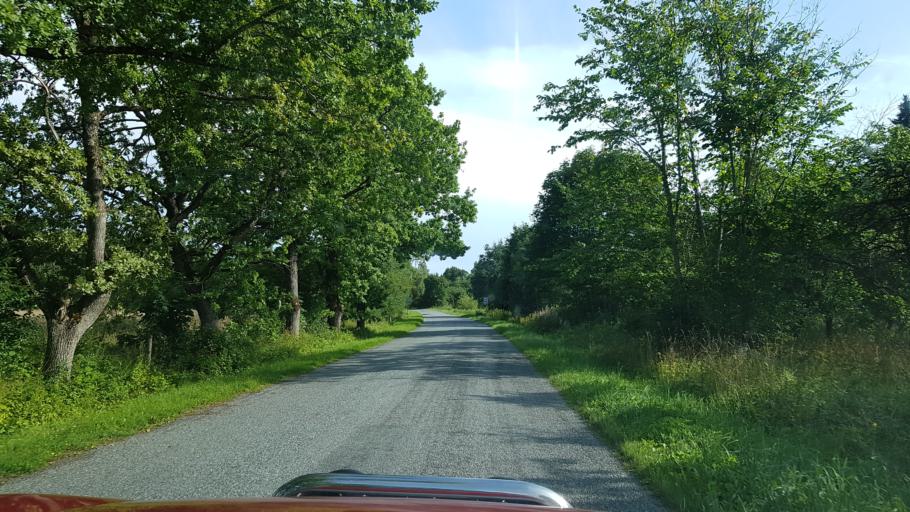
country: EE
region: Laeaene
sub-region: Lihula vald
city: Lihula
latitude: 58.4178
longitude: 24.0105
